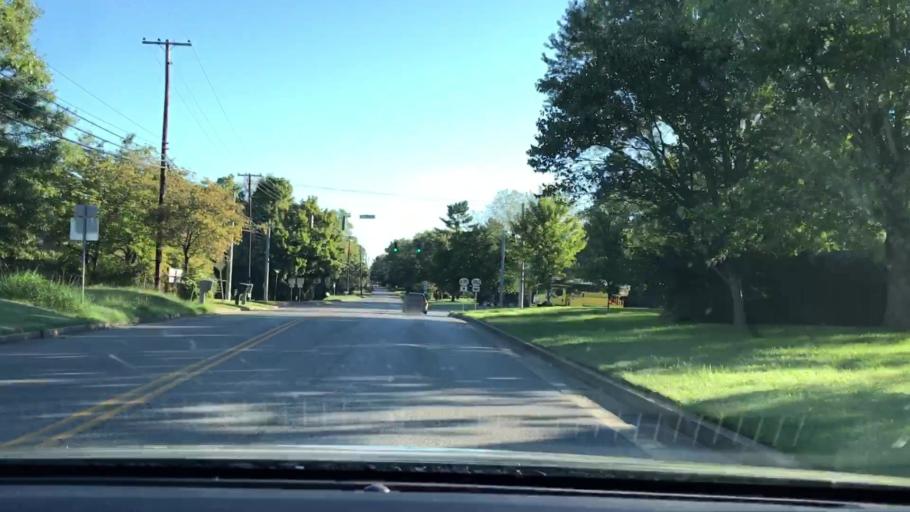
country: US
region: Kentucky
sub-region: Christian County
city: Hopkinsville
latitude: 36.8475
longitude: -87.5124
